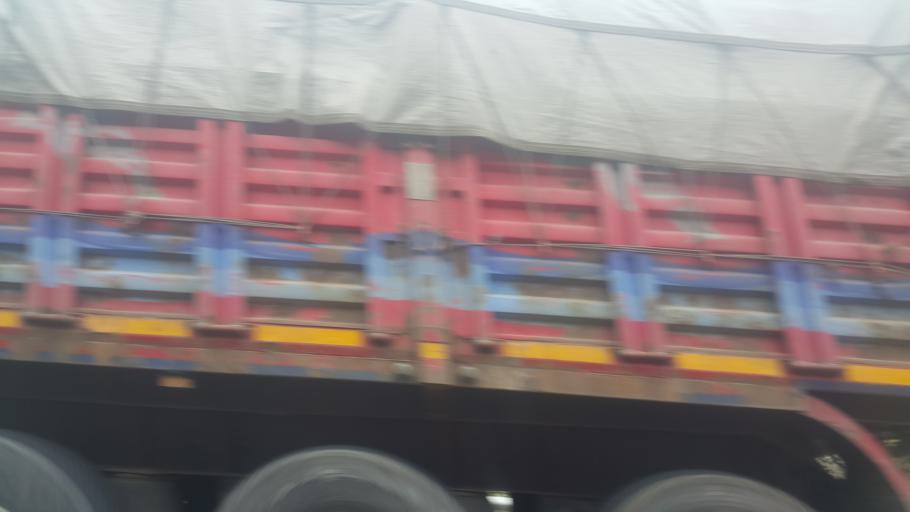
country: TR
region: Adana
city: Pozanti
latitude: 37.4843
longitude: 34.8497
